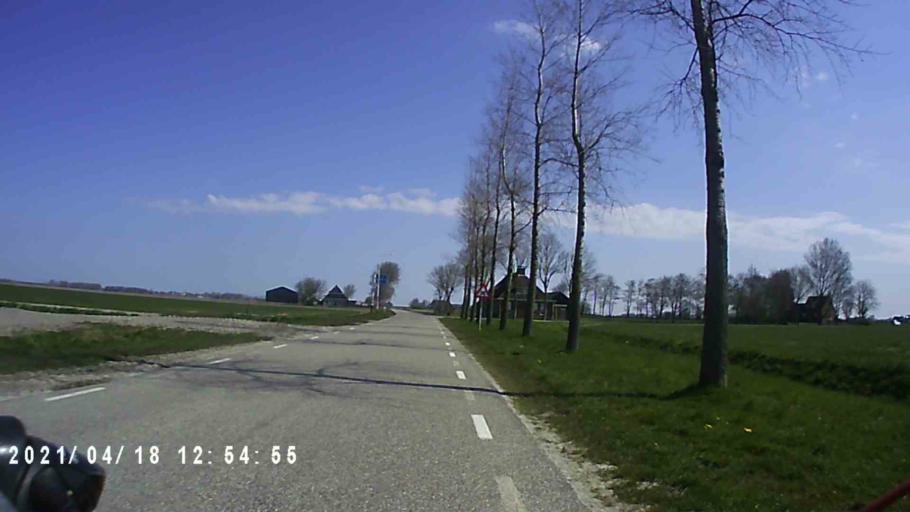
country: NL
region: Friesland
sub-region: Gemeente Dongeradeel
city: Anjum
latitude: 53.3860
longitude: 6.0717
